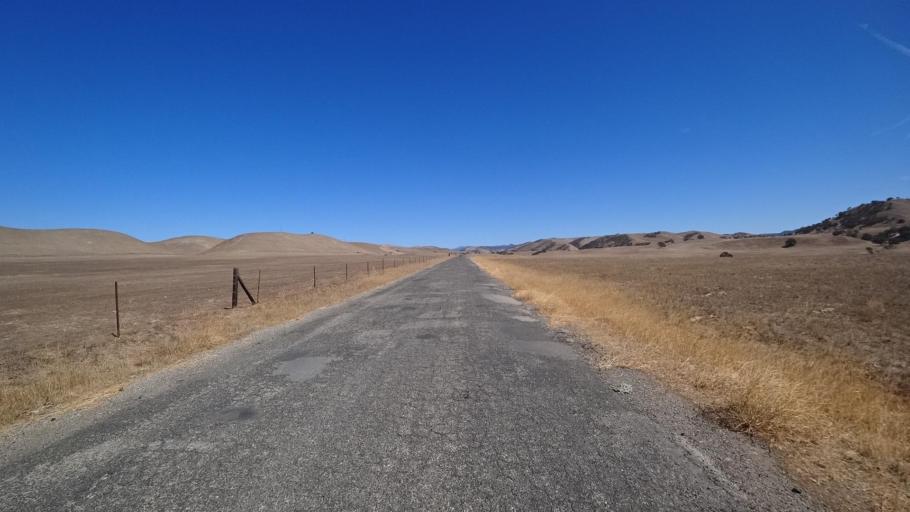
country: US
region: California
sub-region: San Luis Obispo County
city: Lake Nacimiento
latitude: 35.9575
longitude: -120.8440
